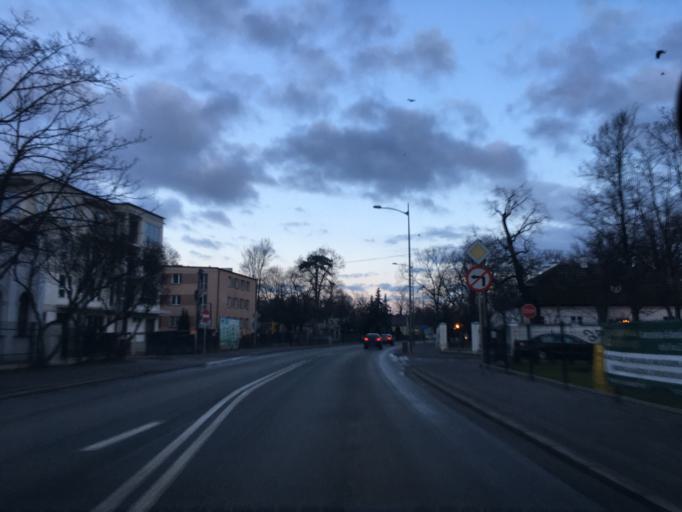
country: PL
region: Masovian Voivodeship
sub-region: Powiat grodziski
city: Grodzisk Mazowiecki
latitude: 52.1051
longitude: 20.6343
